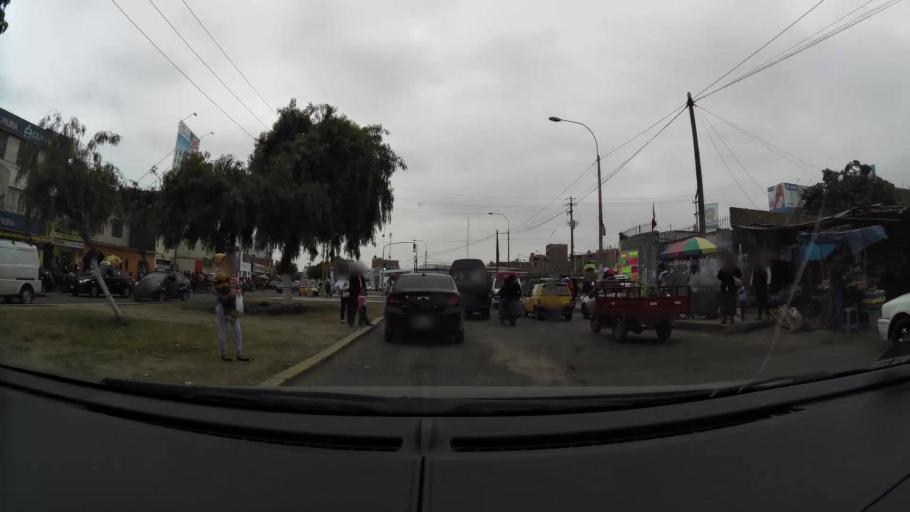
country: PE
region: La Libertad
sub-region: Provincia de Trujillo
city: Trujillo
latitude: -8.0937
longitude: -79.0244
